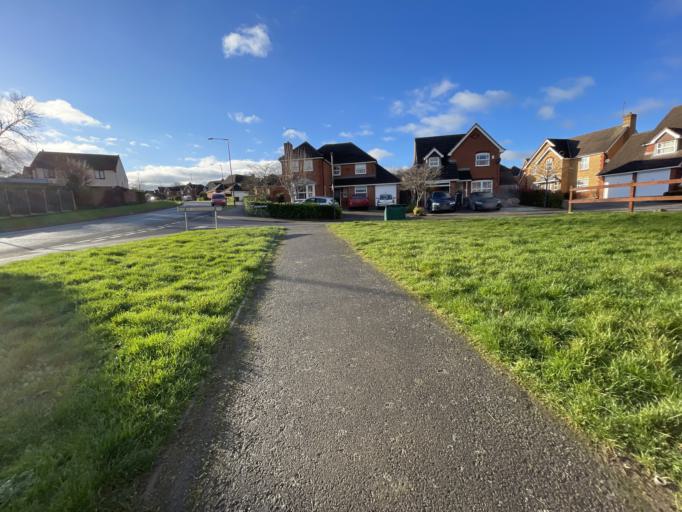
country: GB
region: England
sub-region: Warwickshire
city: Rugby
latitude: 52.3955
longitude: -1.2430
